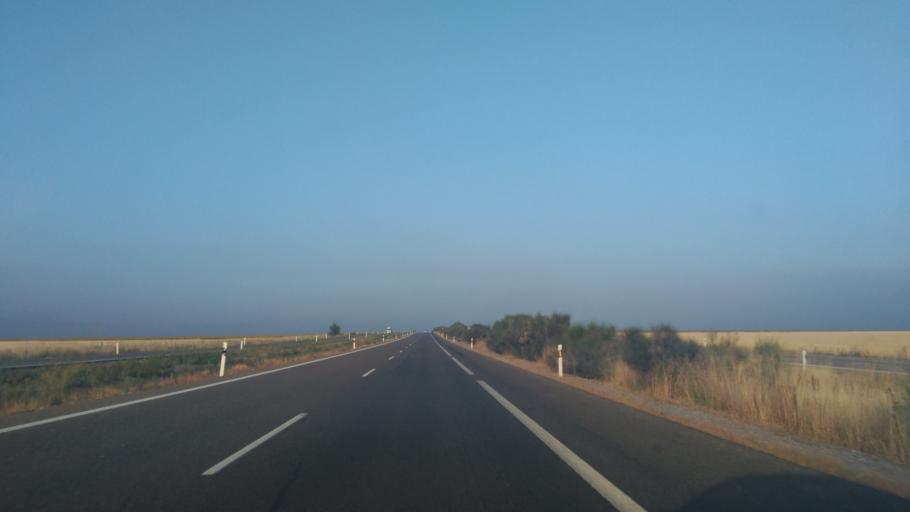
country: ES
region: Castille and Leon
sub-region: Provincia de Salamanca
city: Calzada de Don Diego
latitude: 40.8965
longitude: -5.9204
